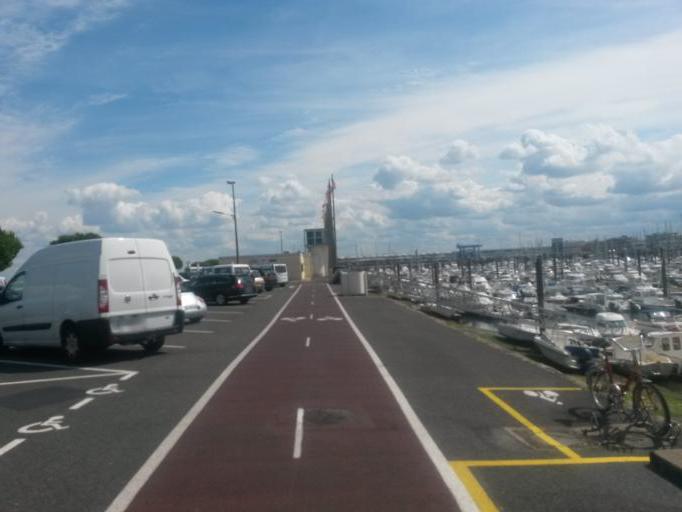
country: FR
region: Aquitaine
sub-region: Departement de la Gironde
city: Arcachon
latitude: 44.6614
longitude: -1.1480
